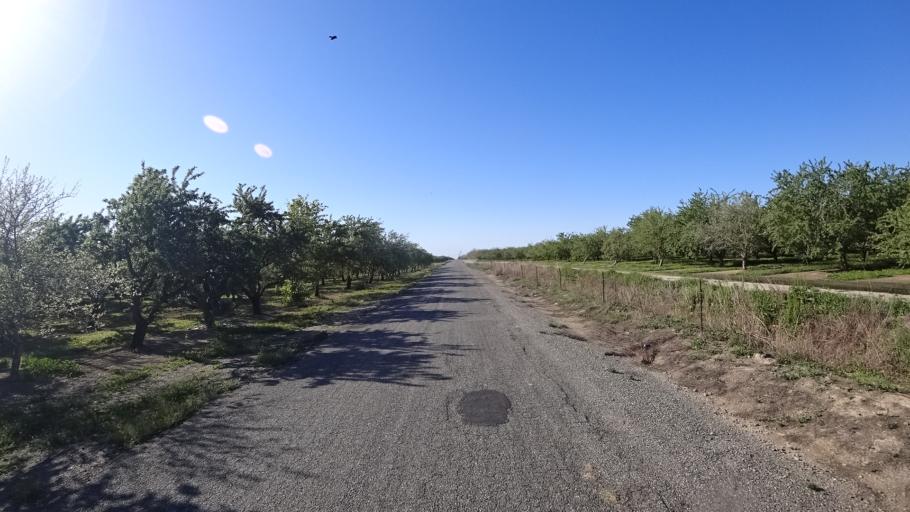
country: US
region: California
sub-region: Glenn County
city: Hamilton City
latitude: 39.7069
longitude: -122.0643
